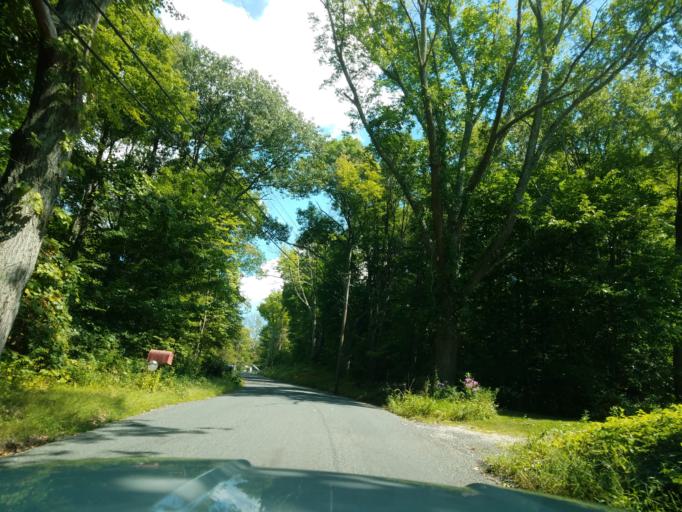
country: US
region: Connecticut
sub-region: Litchfield County
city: Torrington
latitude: 41.7785
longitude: -73.1078
